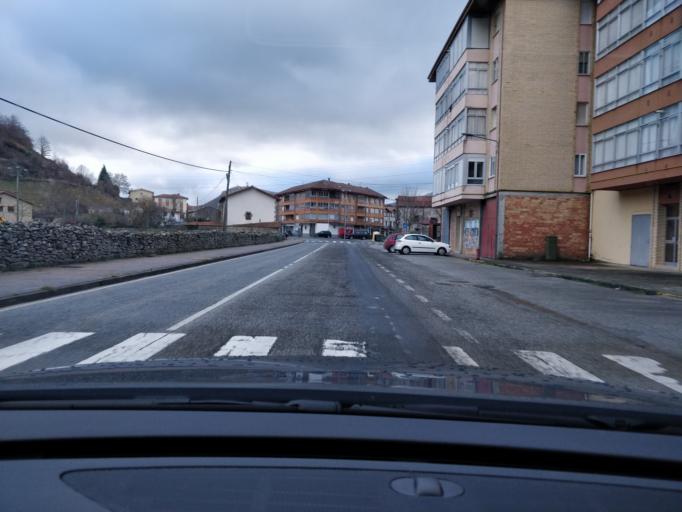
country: ES
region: Castille and Leon
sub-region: Provincia de Burgos
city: Espinosa de los Monteros
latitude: 43.0821
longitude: -3.5568
